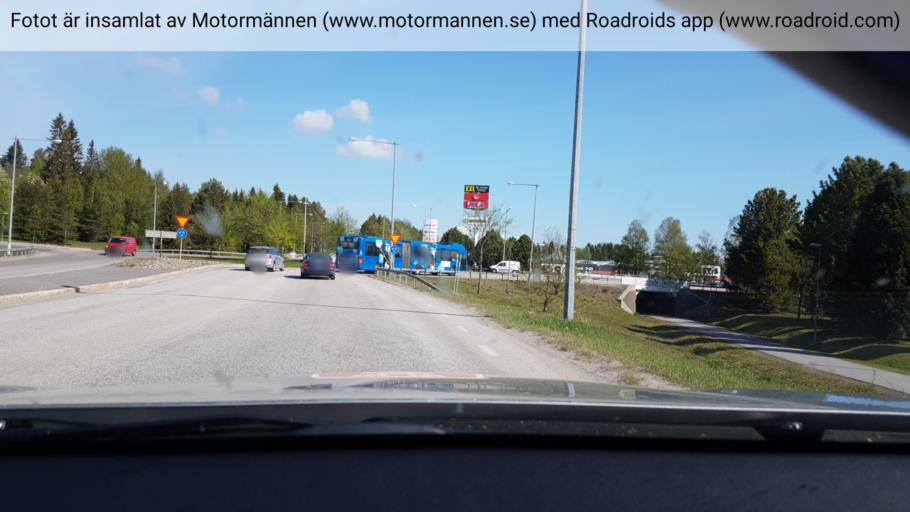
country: SE
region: Vaesterbotten
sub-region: Umea Kommun
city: Ersmark
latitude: 63.8521
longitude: 20.2977
